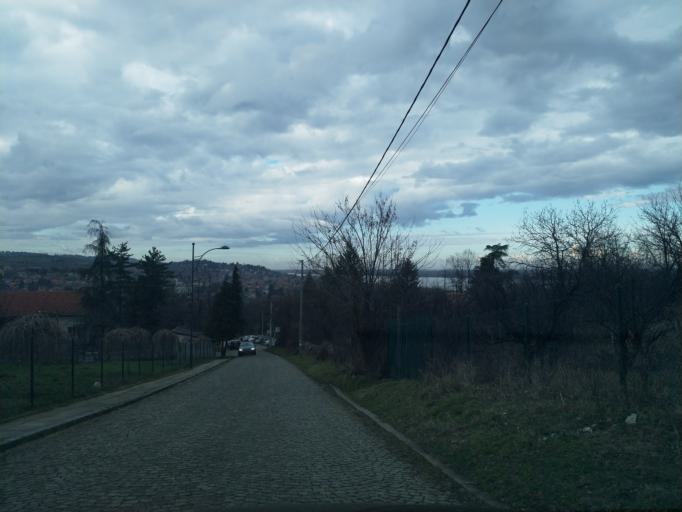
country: RS
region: Central Serbia
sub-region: Belgrade
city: Grocka
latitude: 44.6668
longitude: 20.7209
